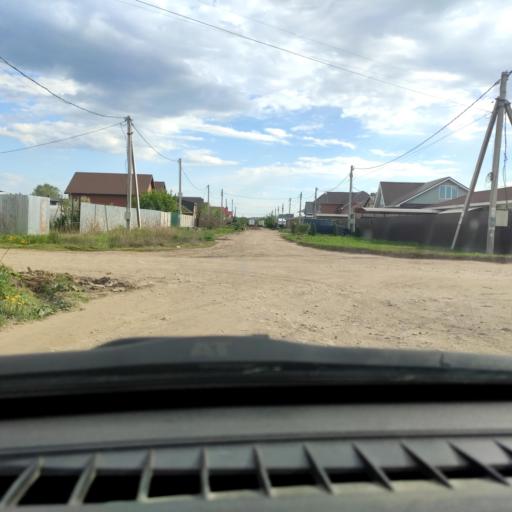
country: RU
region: Samara
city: Tol'yatti
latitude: 53.5688
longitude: 49.4104
